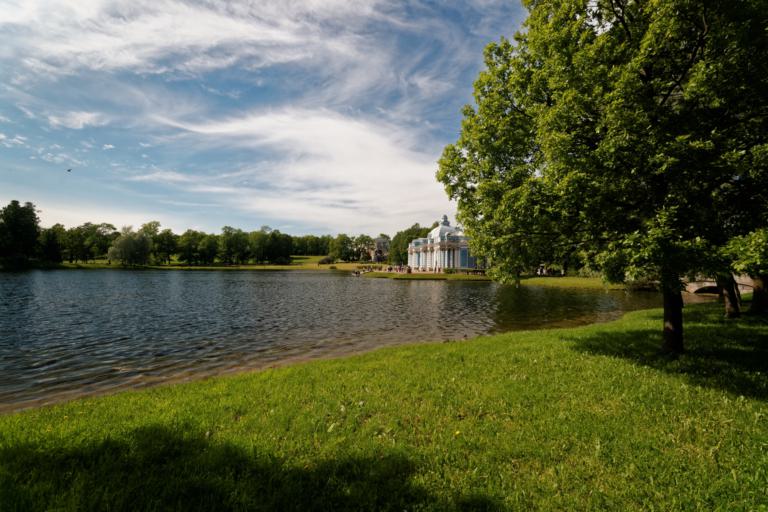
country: RU
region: St.-Petersburg
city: Pushkin
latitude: 59.7127
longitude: 30.3997
